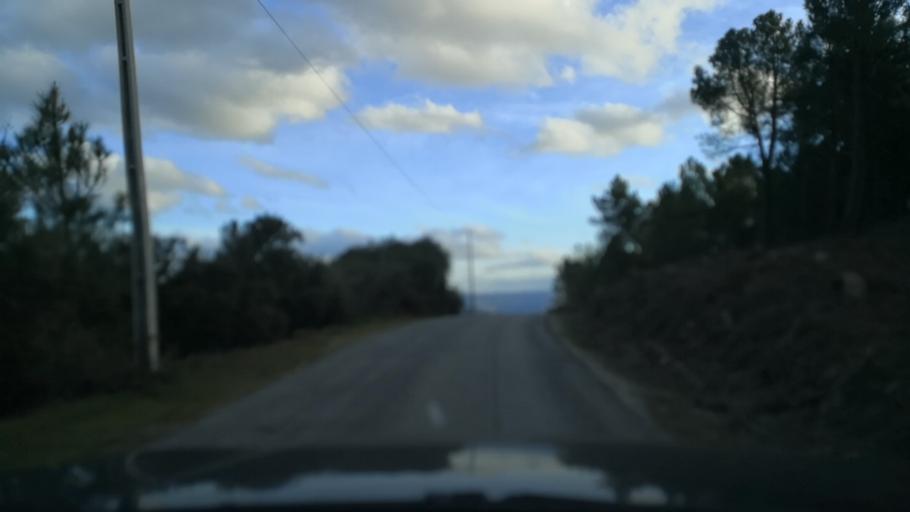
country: PT
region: Braganca
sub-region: Carrazeda de Ansiaes
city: Carrazeda de Anciaes
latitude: 41.2132
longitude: -7.3635
